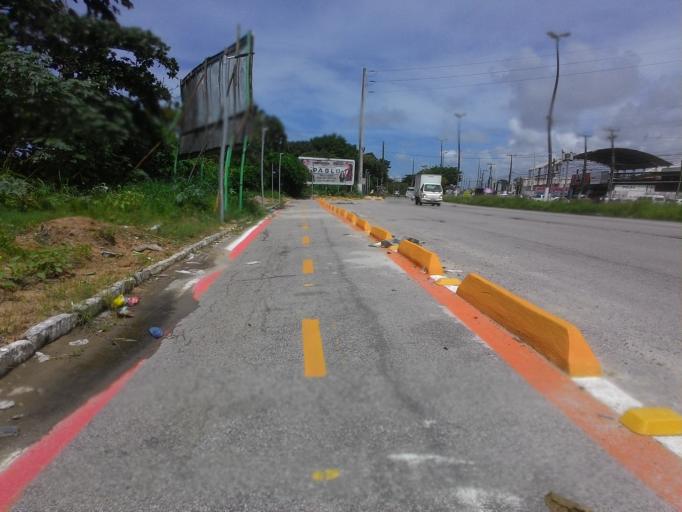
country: BR
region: Pernambuco
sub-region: Olinda
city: Olinda
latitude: -8.0221
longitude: -34.8614
